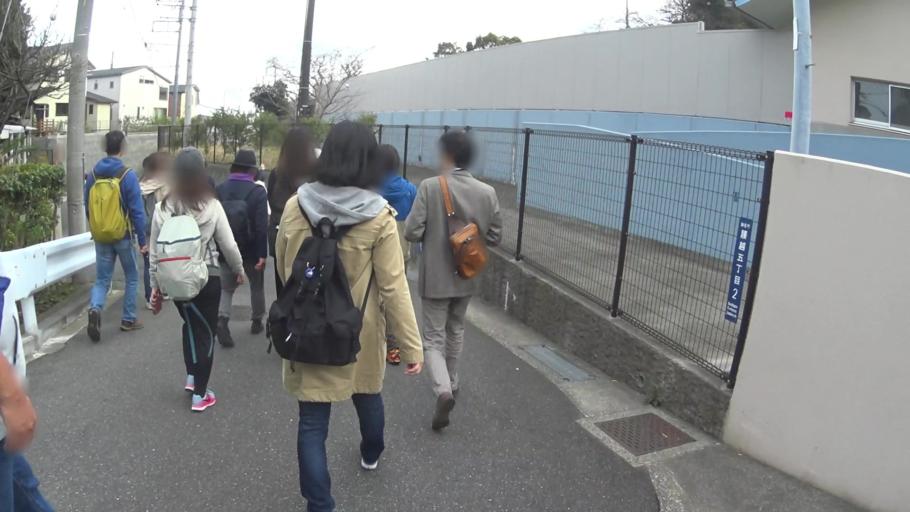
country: JP
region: Kanagawa
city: Fujisawa
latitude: 35.3136
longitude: 139.4914
